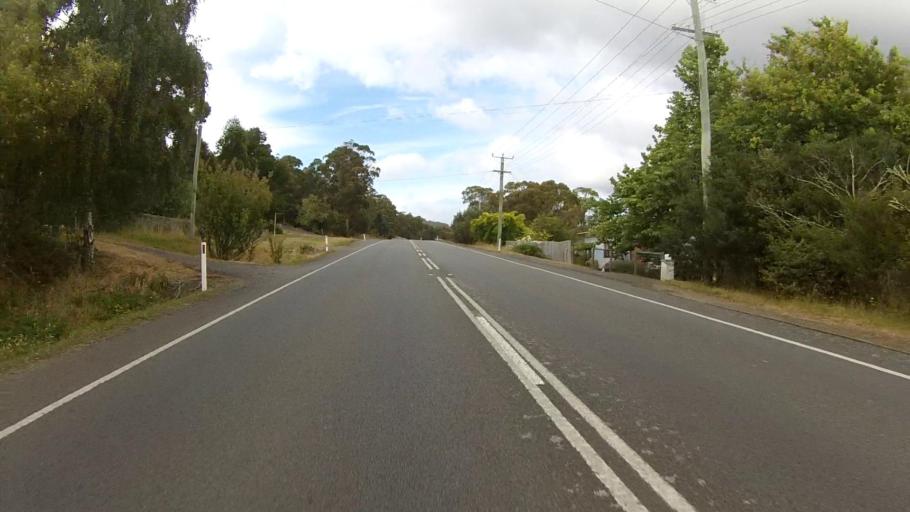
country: AU
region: Tasmania
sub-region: Kingborough
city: Kettering
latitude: -43.0776
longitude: 147.2563
